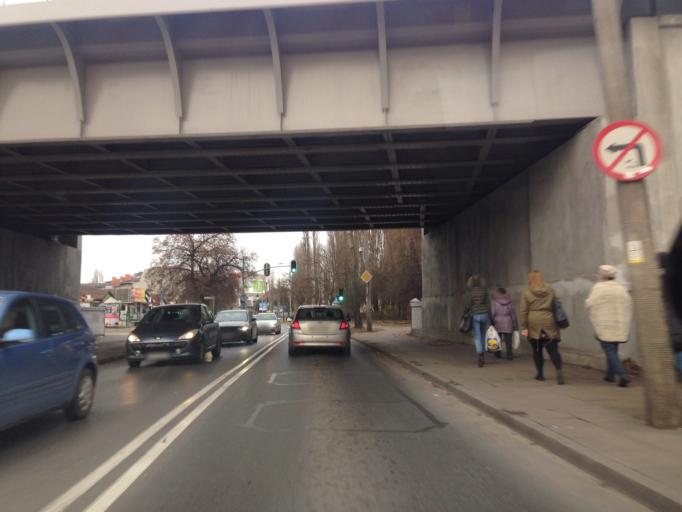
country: PL
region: Pomeranian Voivodeship
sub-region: Gdansk
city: Gdansk
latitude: 54.3779
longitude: 18.6158
